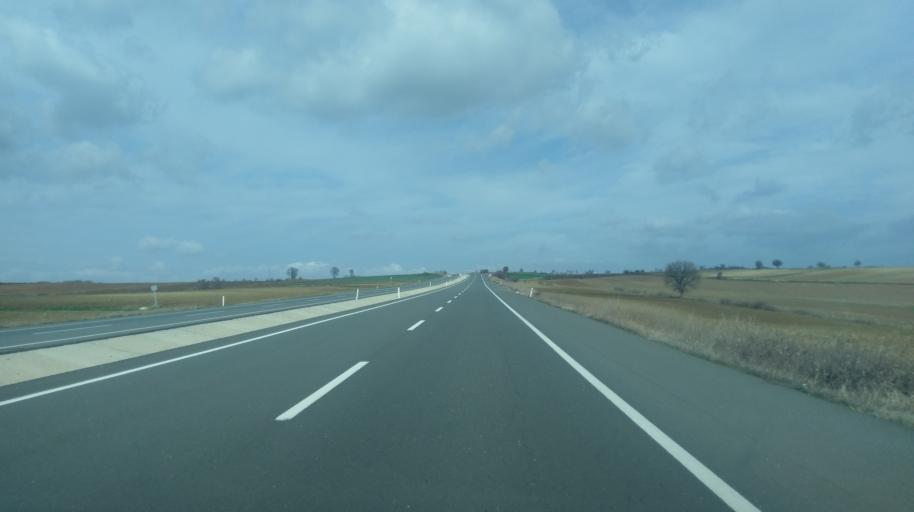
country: TR
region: Edirne
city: Hamidiye
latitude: 41.0538
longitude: 26.6389
